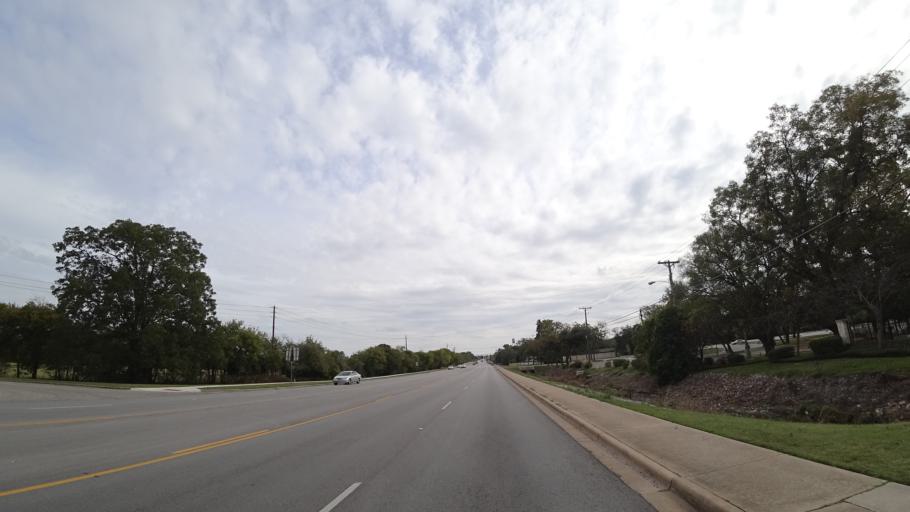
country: US
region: Texas
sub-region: Williamson County
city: Round Rock
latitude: 30.5163
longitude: -97.6823
